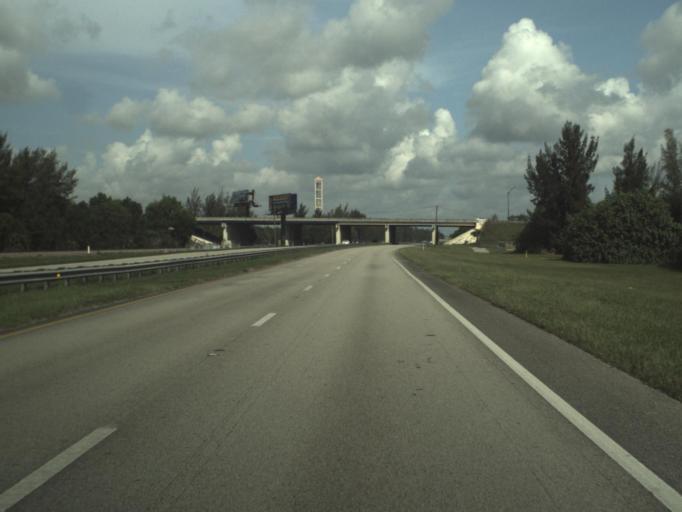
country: US
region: Florida
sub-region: Palm Beach County
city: Palm Beach Gardens
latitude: 26.7942
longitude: -80.1289
